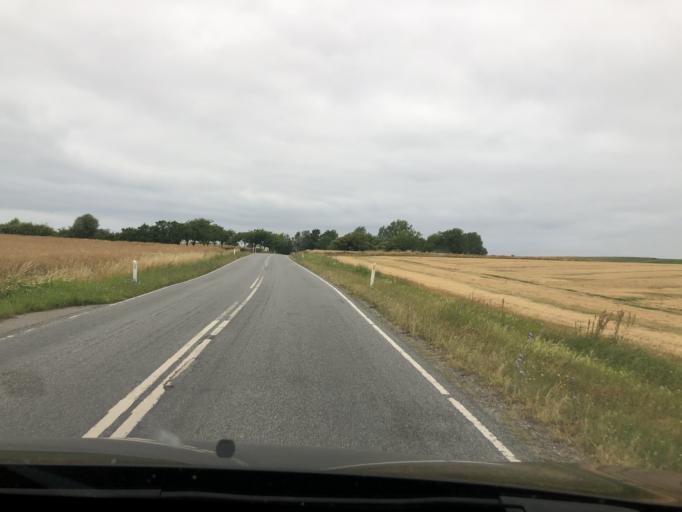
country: DK
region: South Denmark
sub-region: AEro Kommune
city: AEroskobing
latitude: 54.9293
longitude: 10.2676
